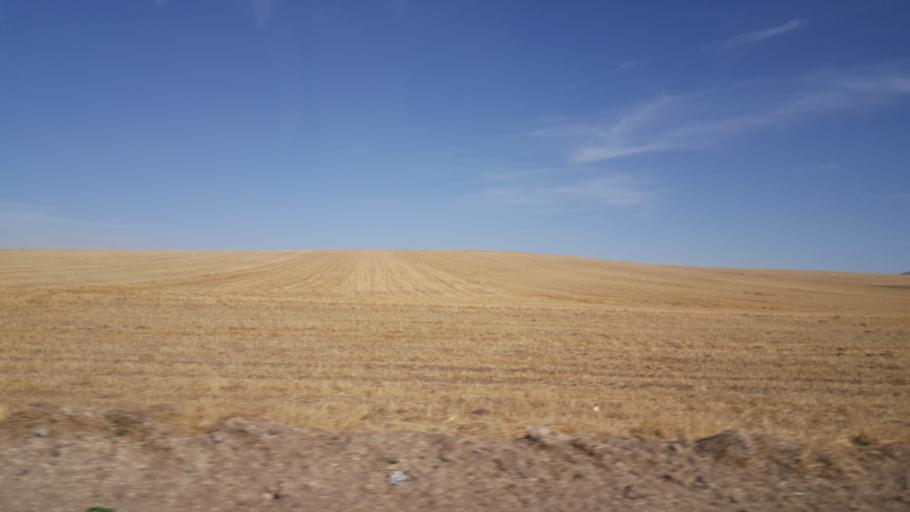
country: TR
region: Ankara
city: Yenice
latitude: 39.3211
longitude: 32.7555
